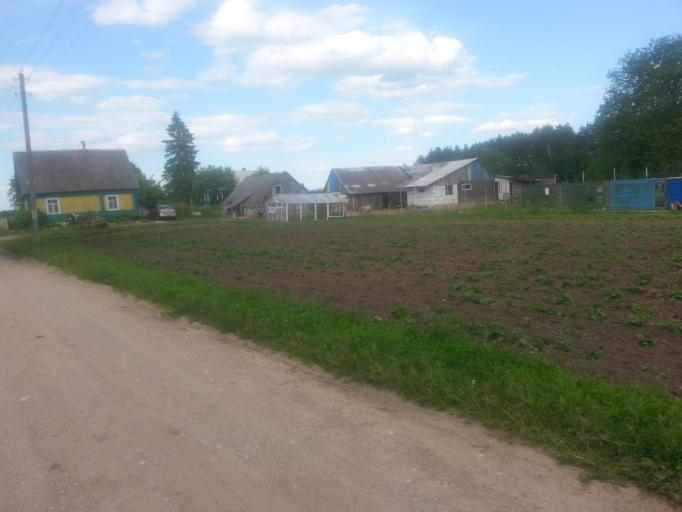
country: BY
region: Minsk
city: Narach
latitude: 54.9776
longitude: 26.6147
